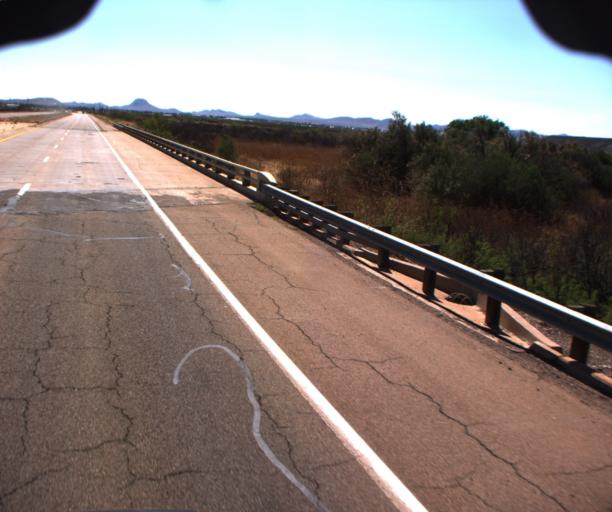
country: US
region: Arizona
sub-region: Cochise County
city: Pirtleville
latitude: 31.3529
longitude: -109.5860
